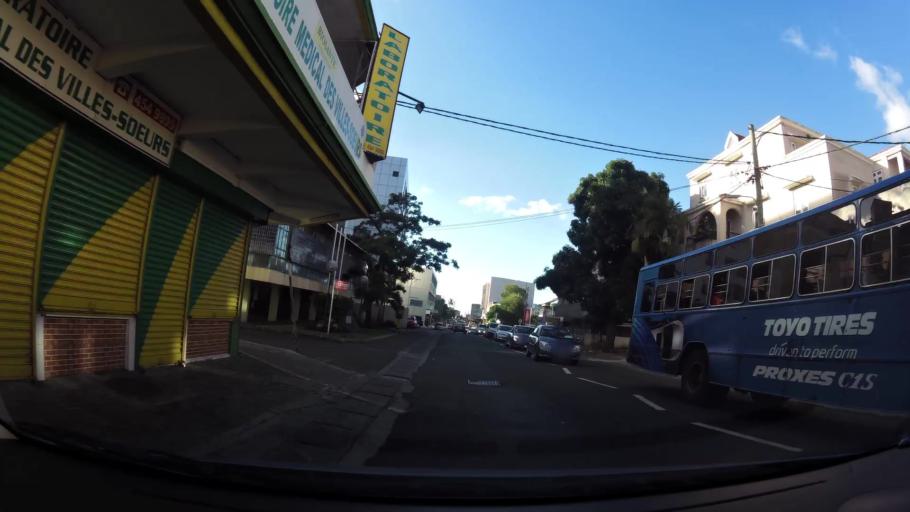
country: MU
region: Plaines Wilhems
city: Ebene
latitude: -20.2289
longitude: 57.4677
